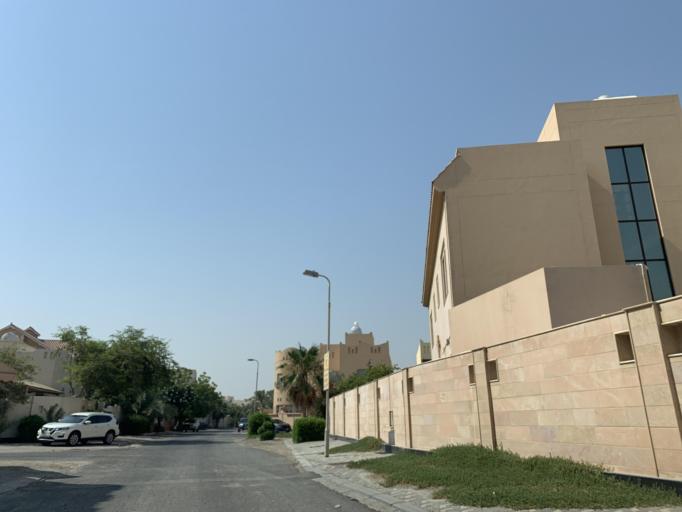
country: BH
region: Manama
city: Jidd Hafs
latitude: 26.1965
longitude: 50.5122
